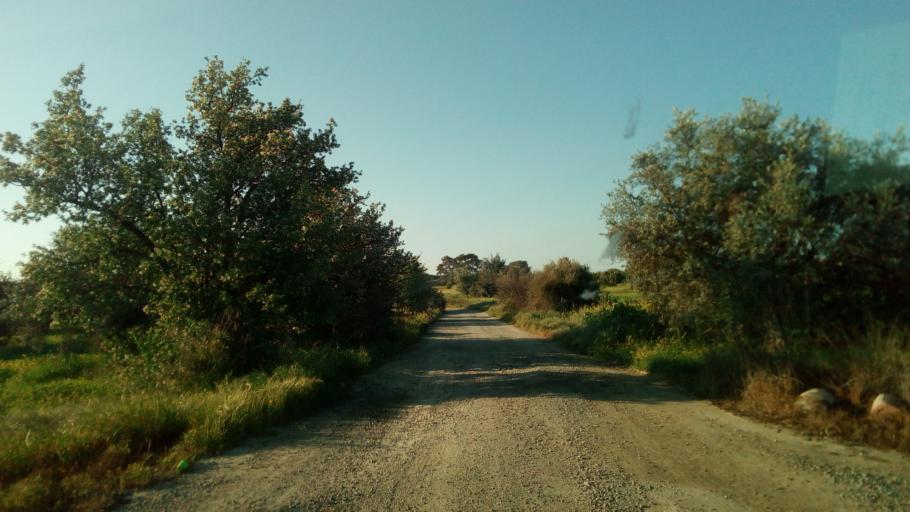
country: CY
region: Larnaka
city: Kofinou
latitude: 34.8492
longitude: 33.4529
